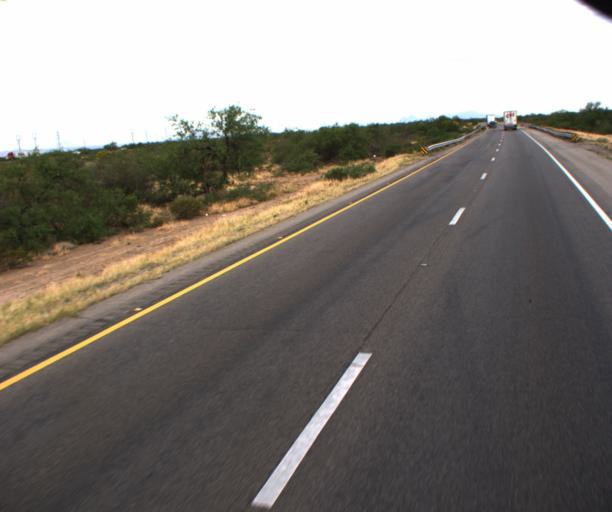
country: US
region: Arizona
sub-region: Pima County
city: Vail
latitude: 32.0414
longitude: -110.7384
